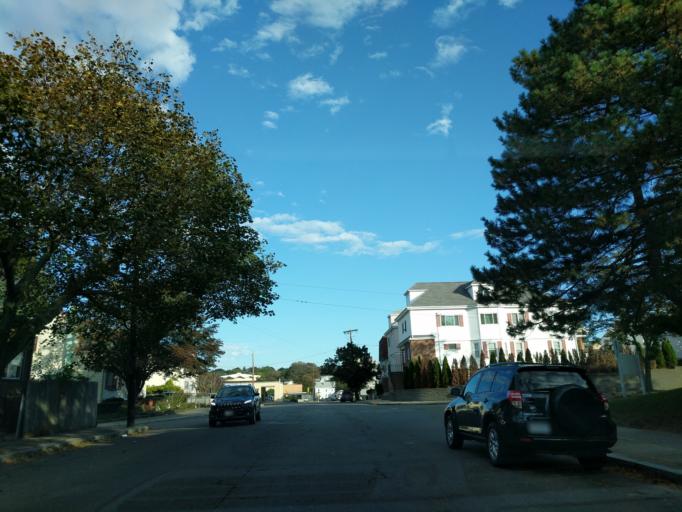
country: US
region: Massachusetts
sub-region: Middlesex County
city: Malden
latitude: 42.4269
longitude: -71.0556
